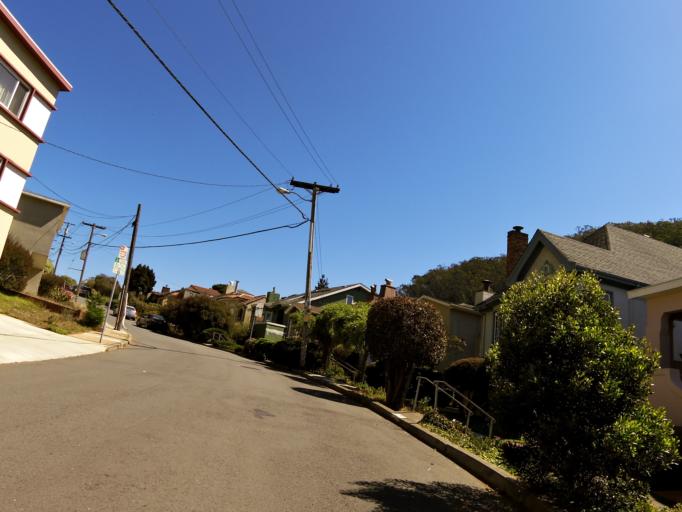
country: US
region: California
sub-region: San Mateo County
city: Daly City
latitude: 37.7410
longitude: -122.4593
